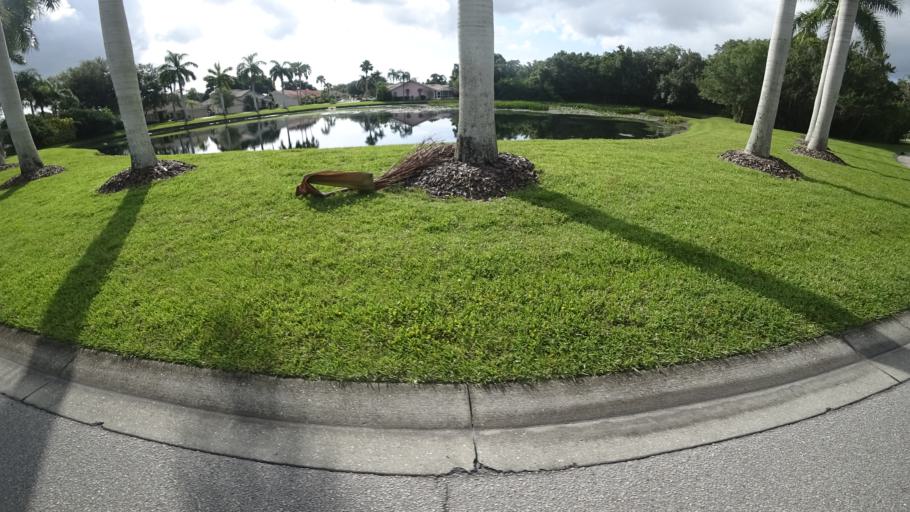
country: US
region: Florida
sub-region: Sarasota County
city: Desoto Lakes
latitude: 27.4149
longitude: -82.4849
